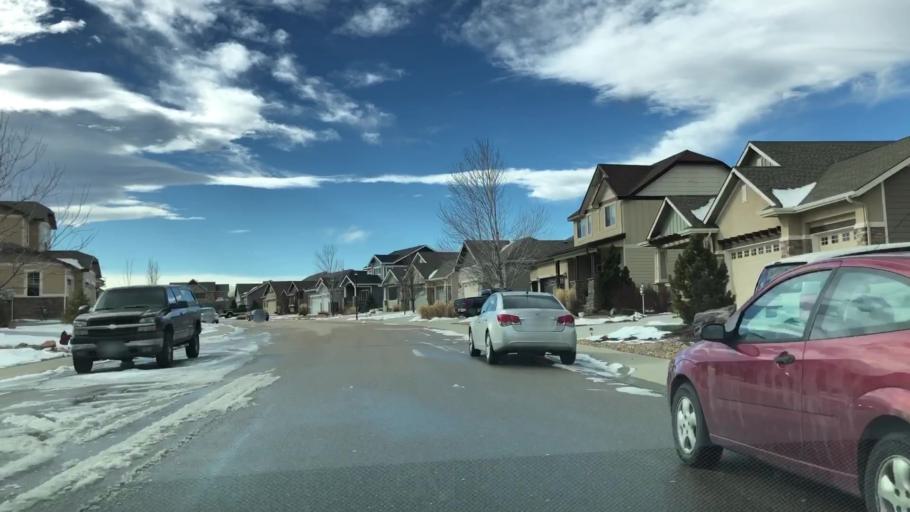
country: US
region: Colorado
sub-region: Weld County
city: Windsor
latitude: 40.4530
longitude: -104.9504
